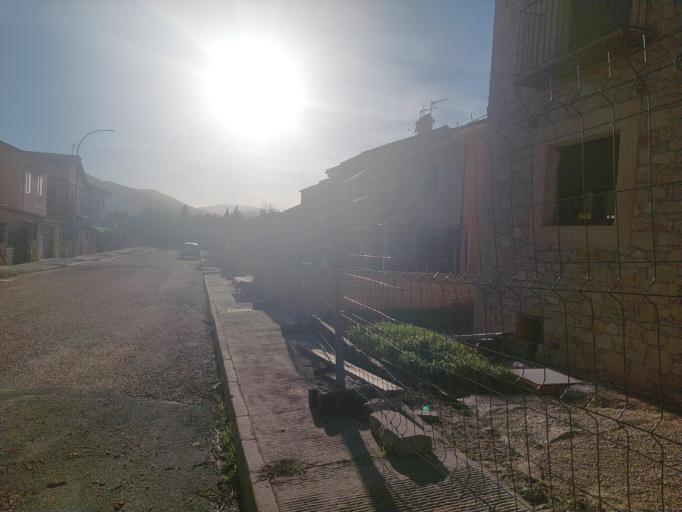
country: ES
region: Castille and Leon
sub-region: Provincia de Segovia
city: Pradena
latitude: 41.1345
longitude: -3.6930
